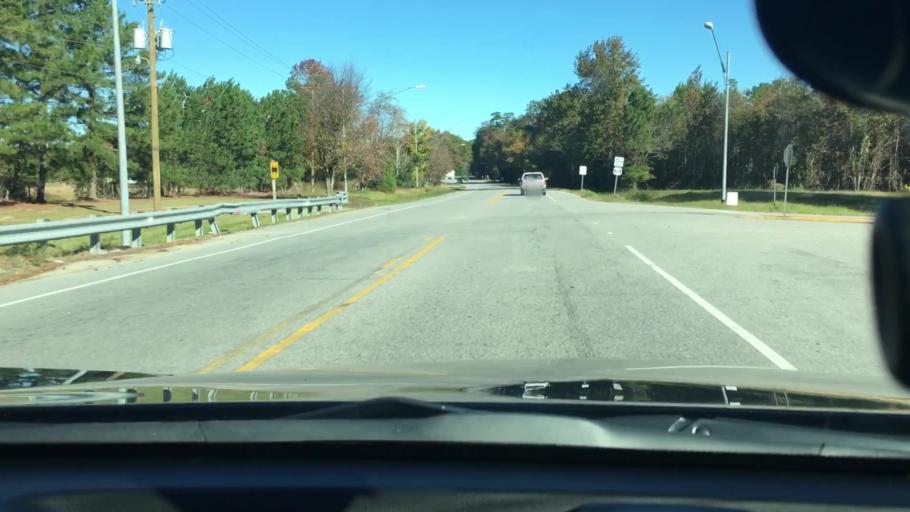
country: US
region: North Carolina
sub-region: Edgecombe County
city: Tarboro
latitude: 35.9138
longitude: -77.5622
